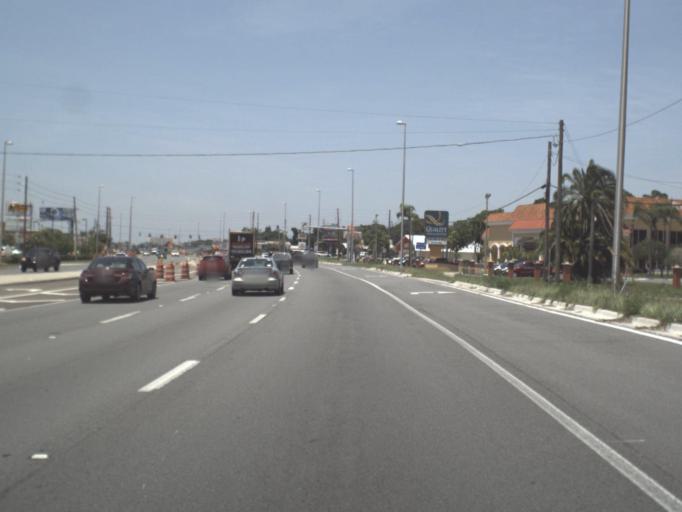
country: US
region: Florida
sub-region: Pasco County
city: New Port Richey
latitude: 28.2356
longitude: -82.7281
